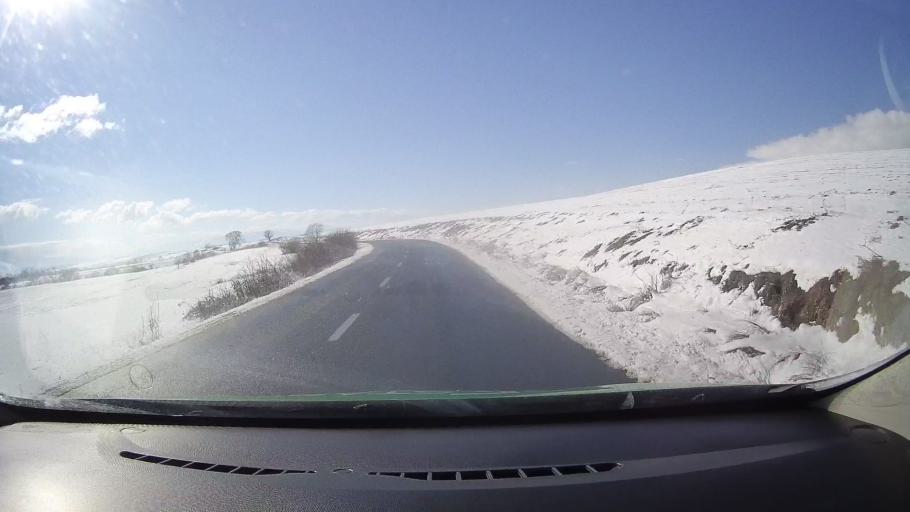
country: RO
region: Sibiu
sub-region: Comuna Rosia
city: Rosia
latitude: 45.8568
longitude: 24.3117
